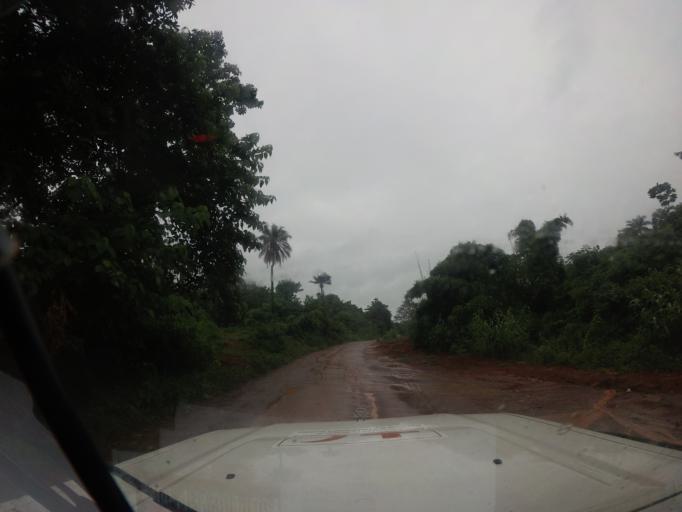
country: SL
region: Northern Province
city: Kabala
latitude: 9.6278
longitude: -11.5500
